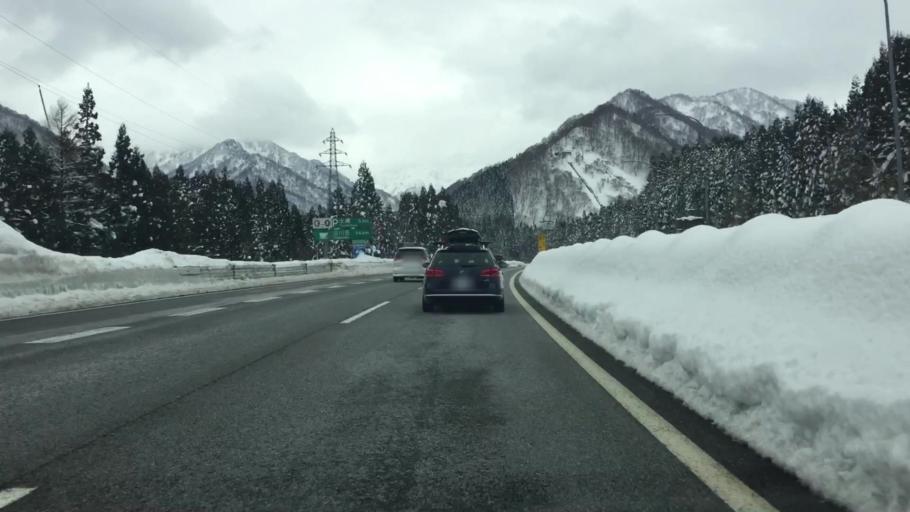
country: JP
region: Niigata
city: Shiozawa
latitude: 36.8850
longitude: 138.8514
